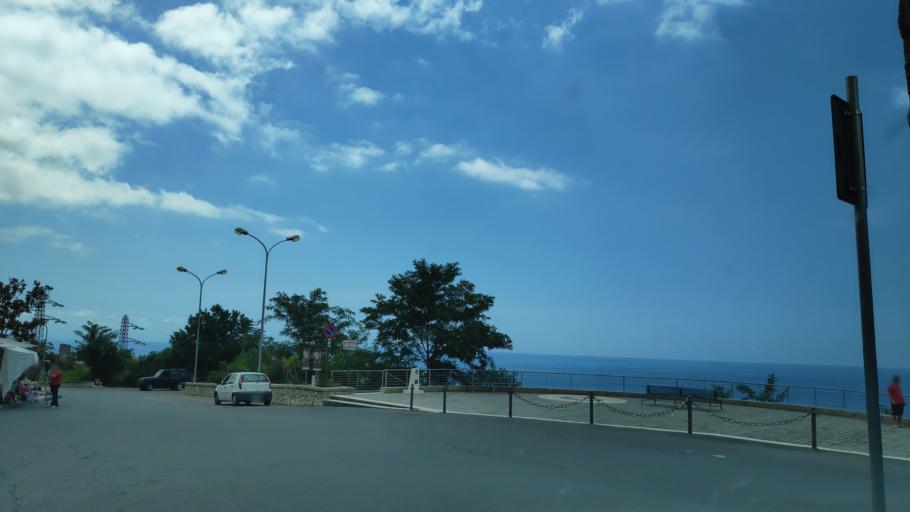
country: IT
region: Calabria
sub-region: Provincia di Cosenza
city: Paola
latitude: 39.3669
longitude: 16.0445
